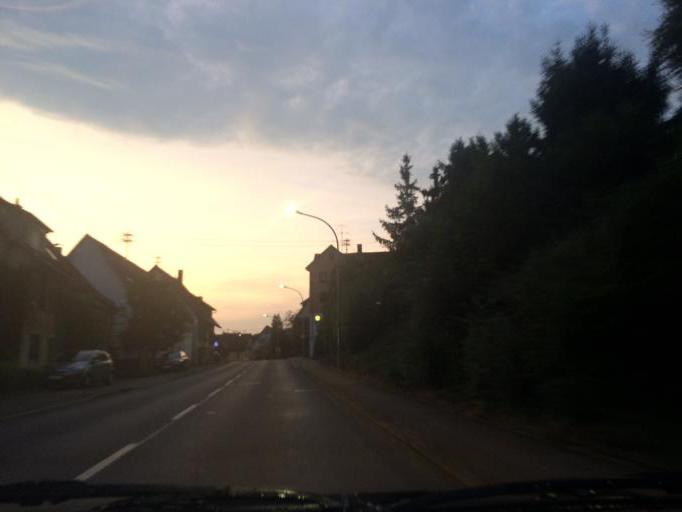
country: DE
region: Baden-Wuerttemberg
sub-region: Regierungsbezirk Stuttgart
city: Schorndorf
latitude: 48.8294
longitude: 9.5134
